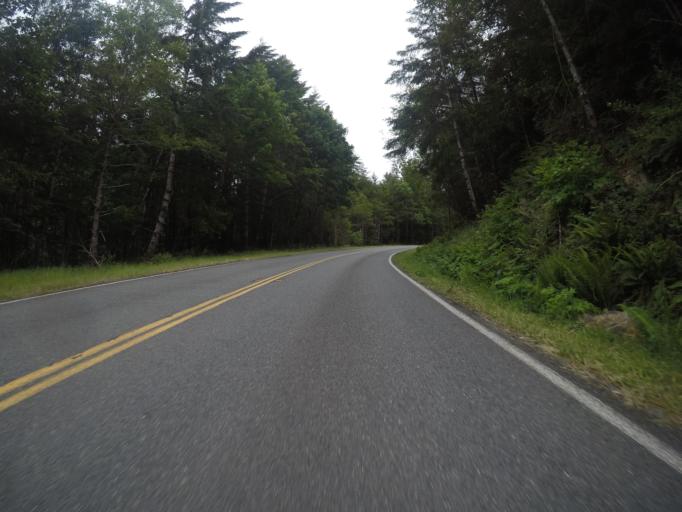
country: US
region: California
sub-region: Del Norte County
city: Bertsch-Oceanview
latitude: 41.7715
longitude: -124.0130
